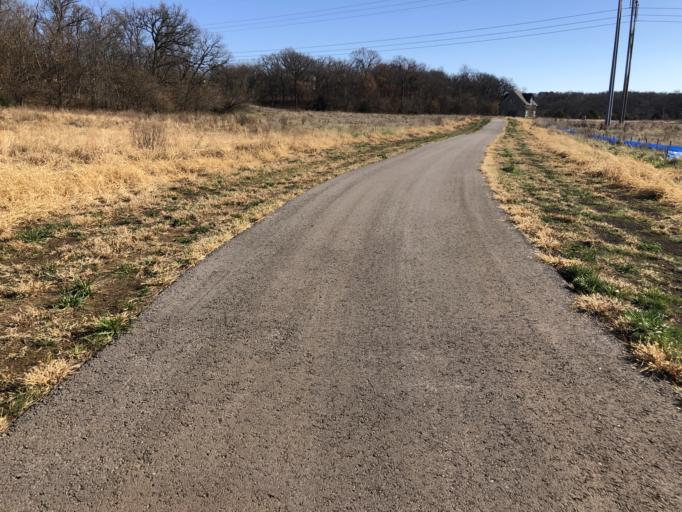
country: US
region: Kansas
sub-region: Johnson County
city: Gardner
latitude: 38.8726
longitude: -94.9514
